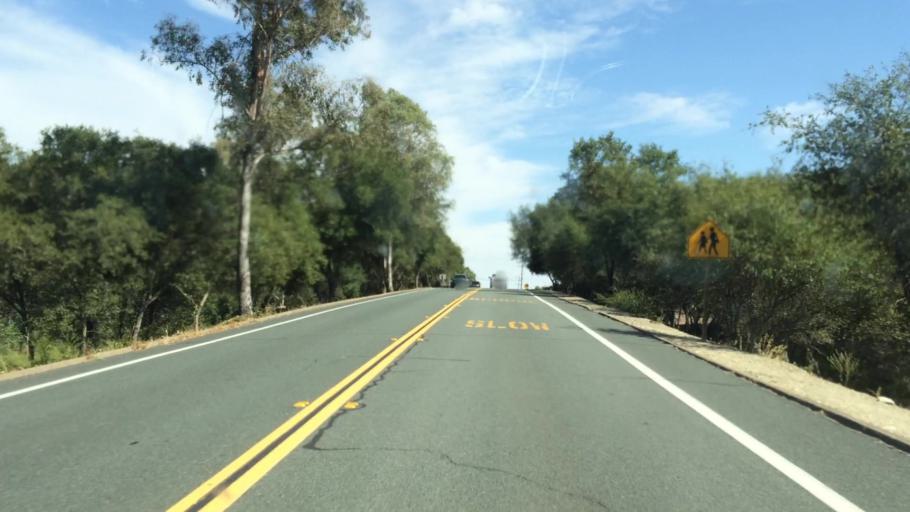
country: US
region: California
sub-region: Amador County
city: Ione
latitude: 38.3607
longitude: -120.9410
